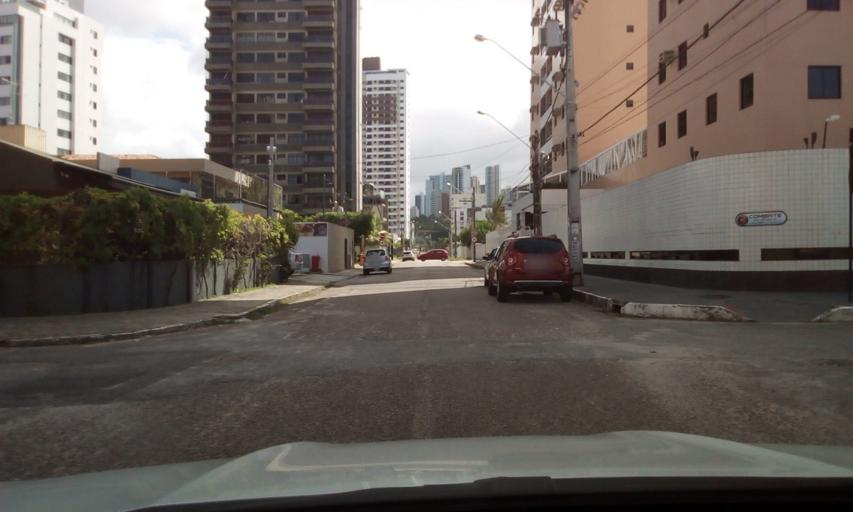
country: BR
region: Paraiba
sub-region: Joao Pessoa
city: Joao Pessoa
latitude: -7.1098
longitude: -34.8290
